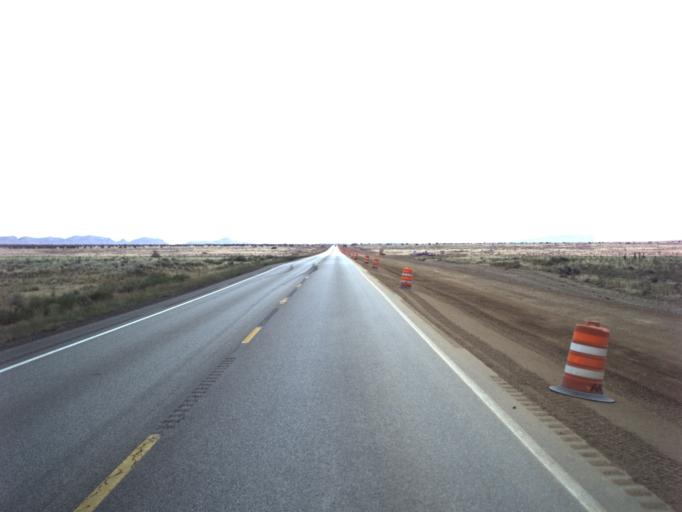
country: US
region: Utah
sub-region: Carbon County
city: East Carbon City
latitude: 39.4406
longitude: -110.4638
